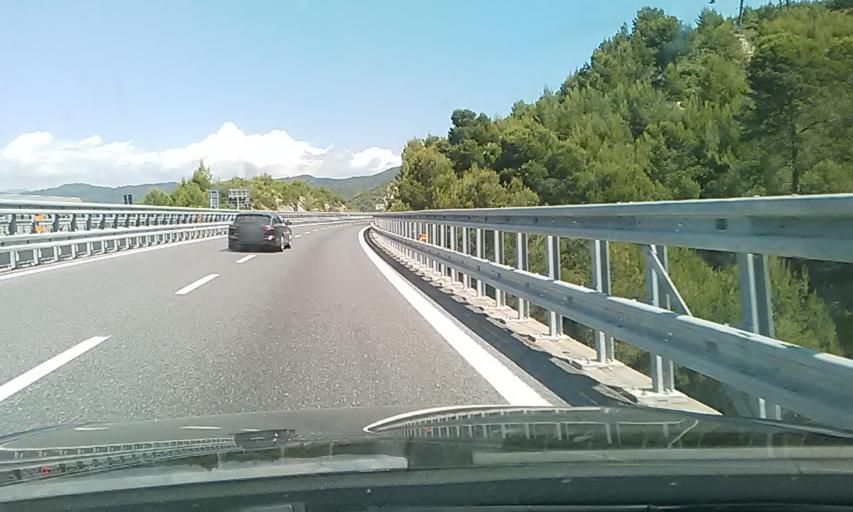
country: IT
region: Liguria
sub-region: Provincia di Savona
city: Laigueglia
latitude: 43.9823
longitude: 8.1374
